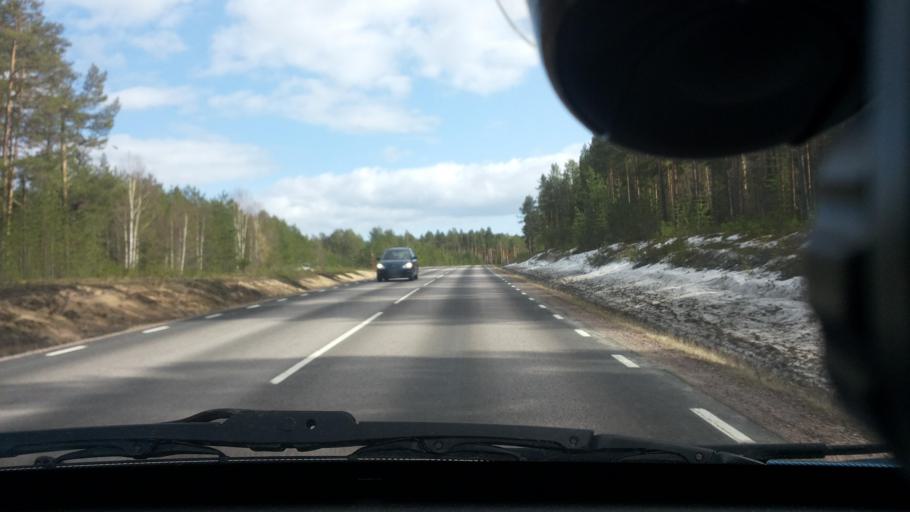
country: SE
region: Norrbotten
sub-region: Lulea Kommun
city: Sodra Sunderbyn
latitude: 65.6367
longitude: 21.9137
